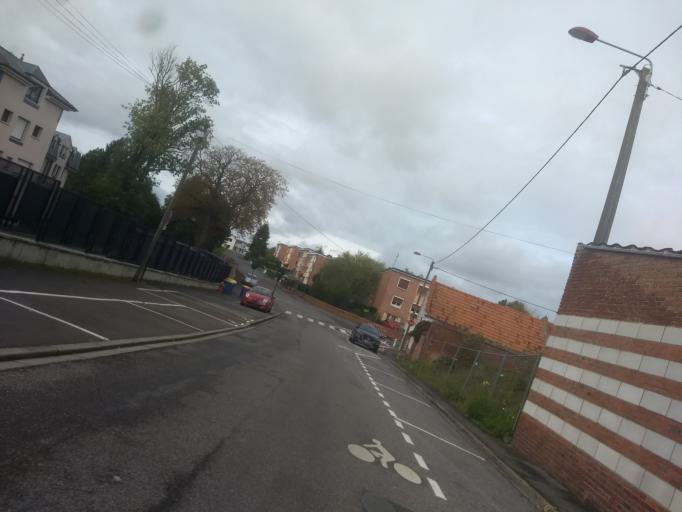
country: FR
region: Nord-Pas-de-Calais
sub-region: Departement du Pas-de-Calais
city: Anzin-Saint-Aubin
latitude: 50.3126
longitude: 2.7443
